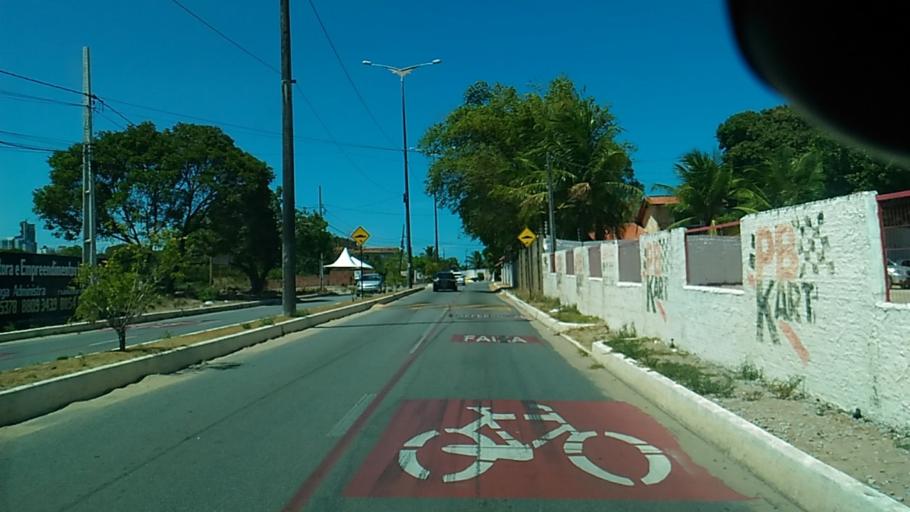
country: BR
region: Paraiba
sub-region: Joao Pessoa
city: Joao Pessoa
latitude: -7.1455
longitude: -34.8171
